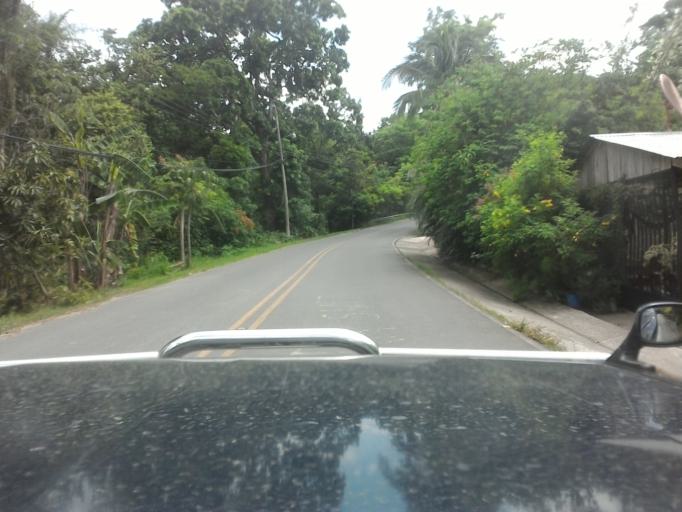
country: CR
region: Guanacaste
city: Juntas
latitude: 10.1991
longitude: -84.8444
